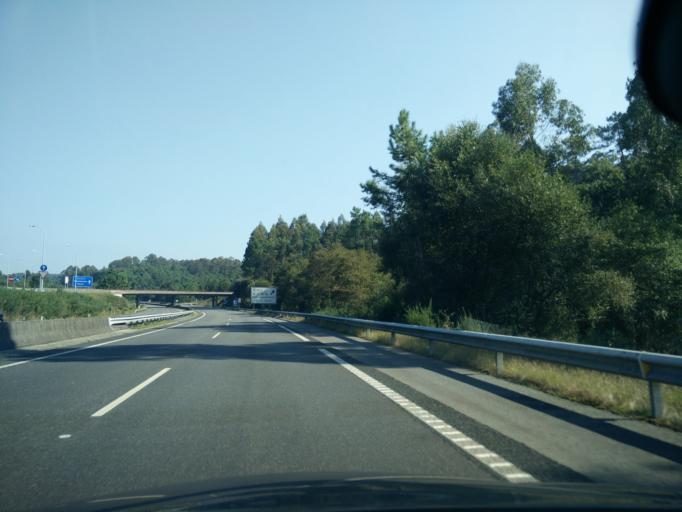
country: ES
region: Galicia
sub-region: Provincia da Coruna
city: Mino
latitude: 43.3727
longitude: -8.1877
